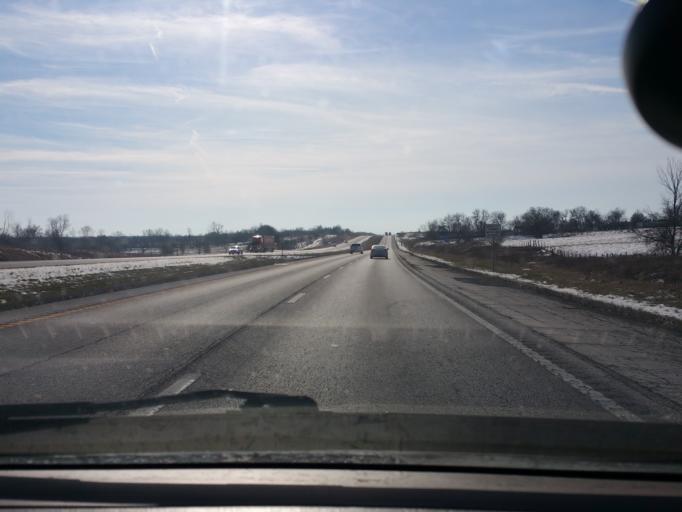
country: US
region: Missouri
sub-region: Clinton County
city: Cameron
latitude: 39.7272
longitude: -94.2210
